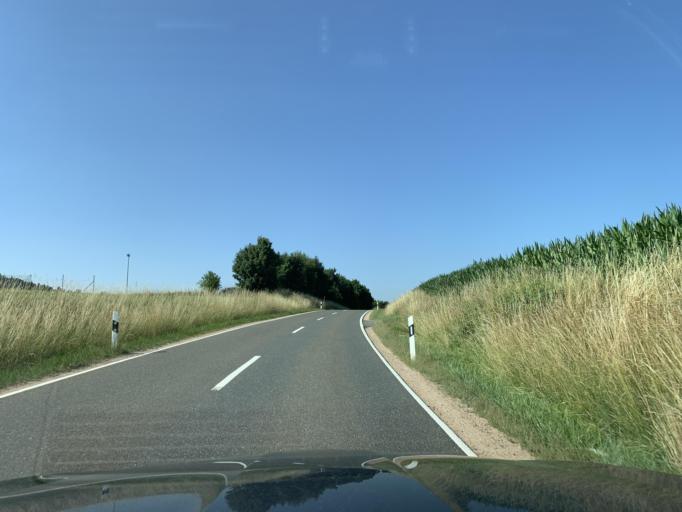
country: DE
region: Bavaria
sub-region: Upper Palatinate
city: Schwarzhofen
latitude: 49.3848
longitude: 12.3515
